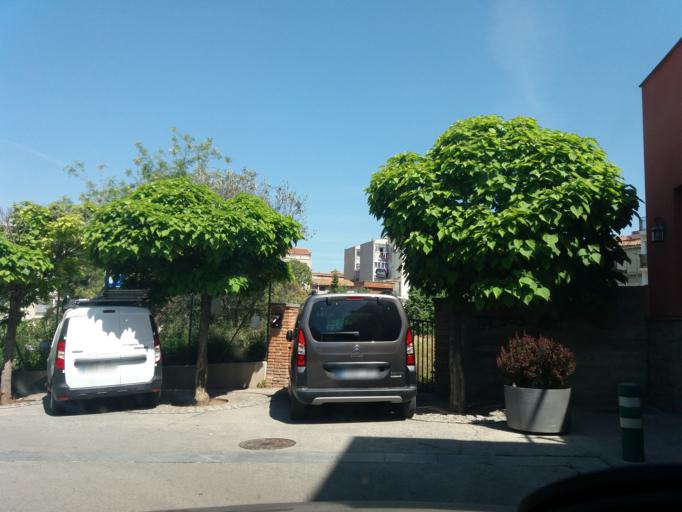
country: ES
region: Catalonia
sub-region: Provincia de Barcelona
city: Manresa
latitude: 41.7223
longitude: 1.8334
